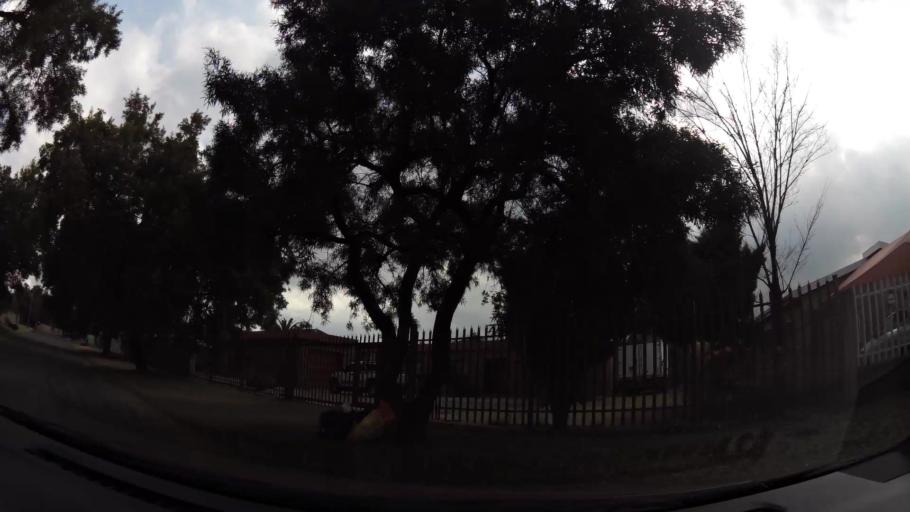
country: ZA
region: Gauteng
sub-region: Sedibeng District Municipality
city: Vanderbijlpark
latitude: -26.7215
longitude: 27.8502
